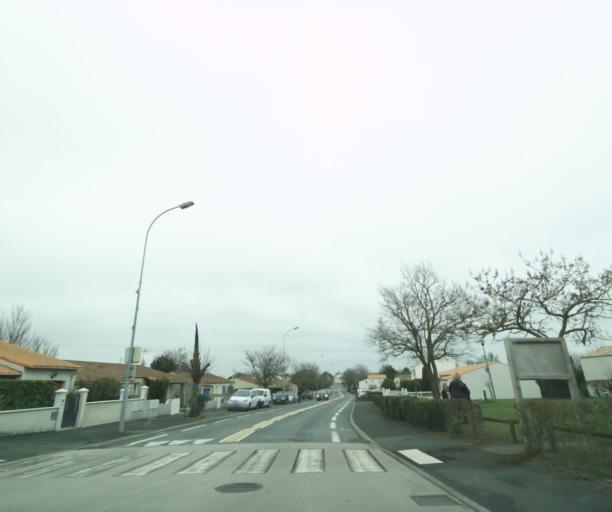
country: FR
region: Poitou-Charentes
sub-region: Departement de la Charente-Maritime
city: Lagord
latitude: 46.1842
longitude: -1.1425
